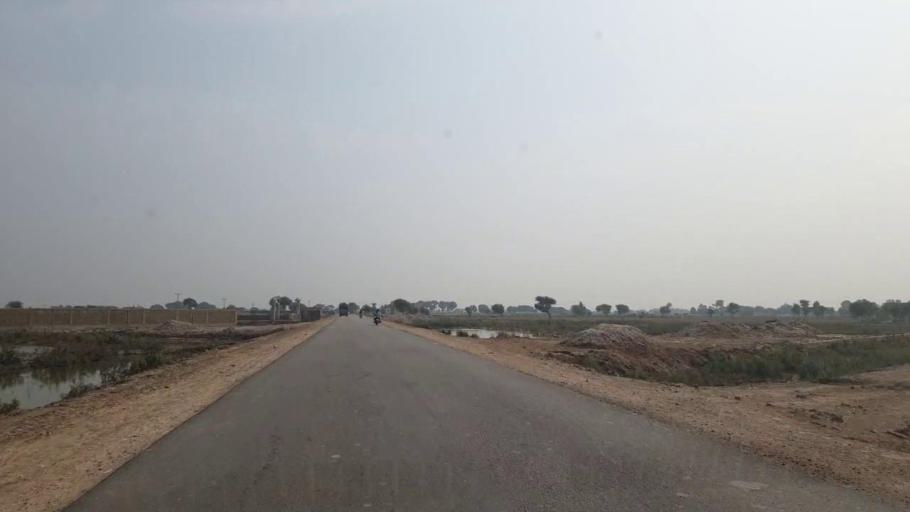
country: PK
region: Sindh
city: Matli
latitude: 25.0550
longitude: 68.6763
